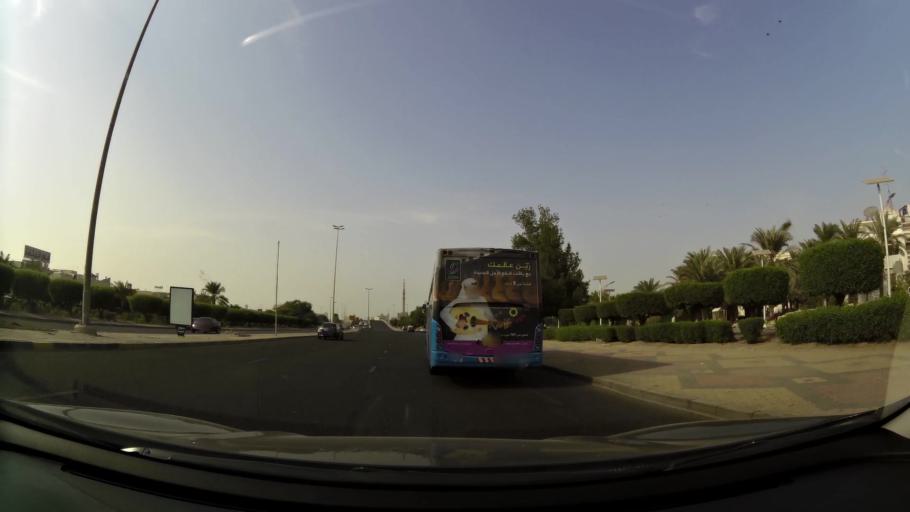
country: KW
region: Al Asimah
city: Ash Shamiyah
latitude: 29.3305
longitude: 47.9544
